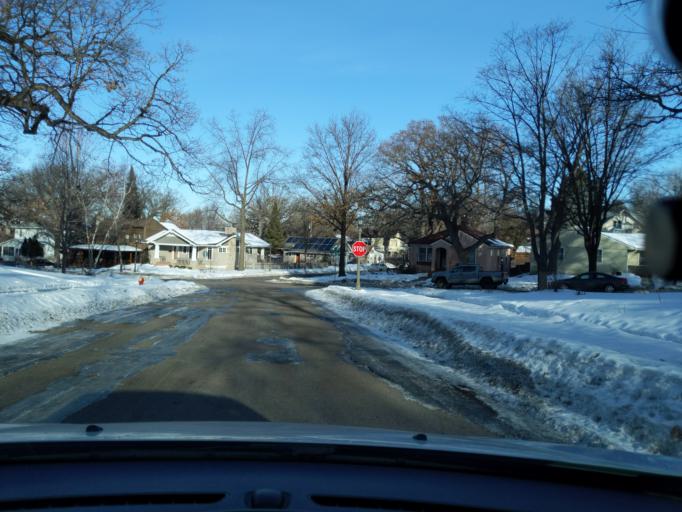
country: US
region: Minnesota
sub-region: Ramsey County
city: Lauderdale
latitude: 44.9831
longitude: -93.1992
